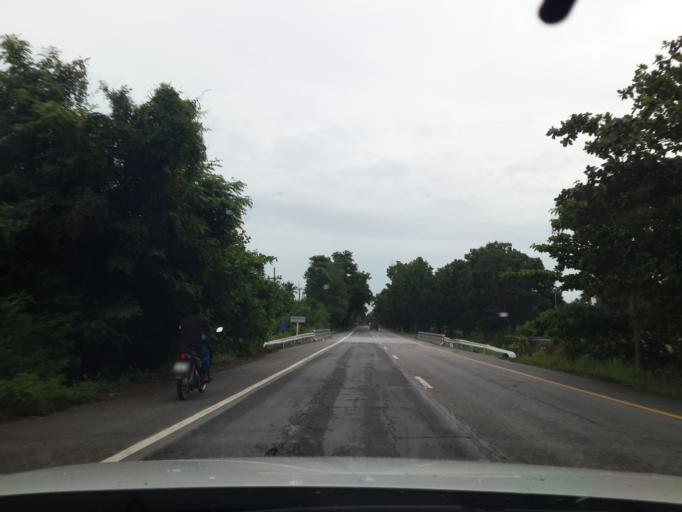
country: TH
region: Songkhla
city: Thepha
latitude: 6.8401
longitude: 101.0075
